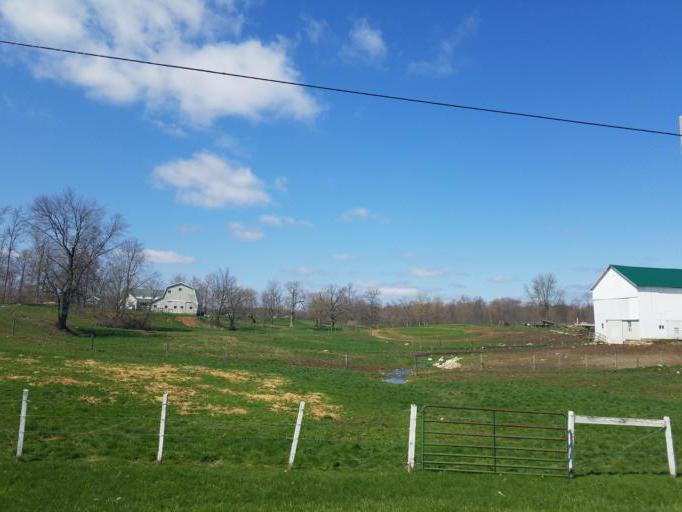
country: US
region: Ohio
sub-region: Geauga County
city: Middlefield
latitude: 41.4039
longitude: -81.0802
